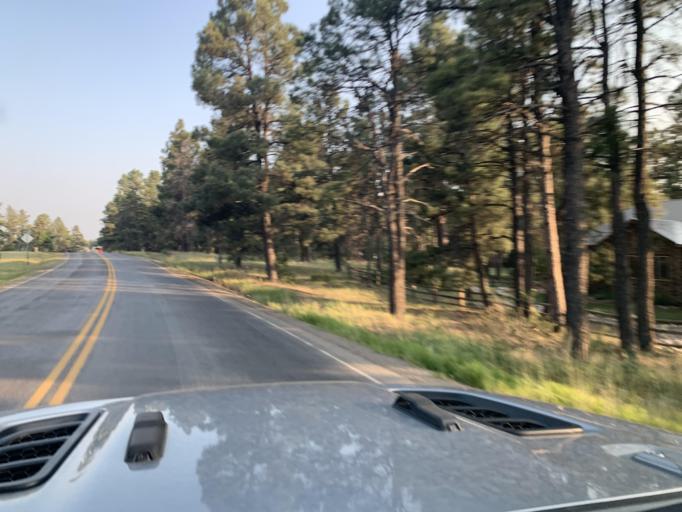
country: US
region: Colorado
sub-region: Archuleta County
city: Pagosa Springs
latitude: 37.2731
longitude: -107.0976
